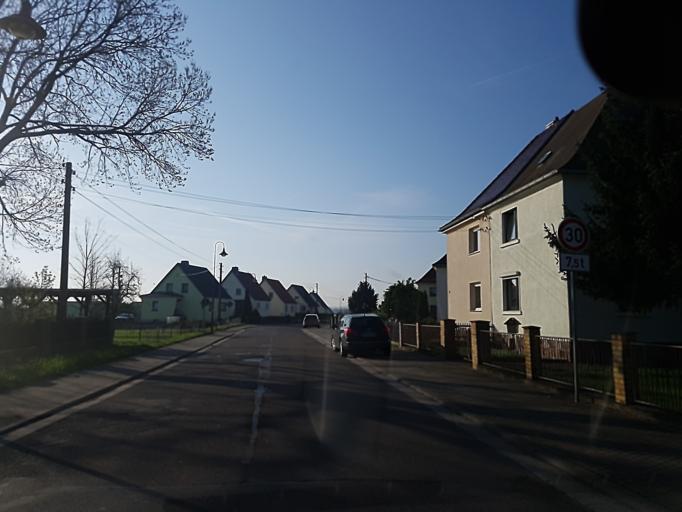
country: DE
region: Saxony
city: Mugeln
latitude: 51.2437
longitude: 13.0373
